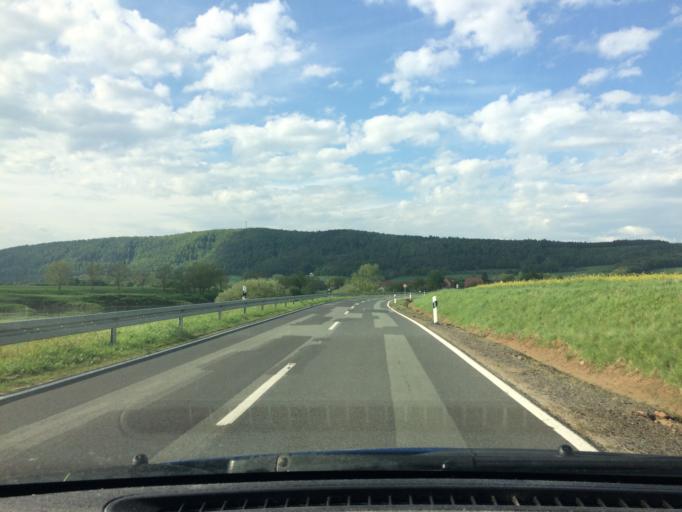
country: DE
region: Lower Saxony
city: Bodenfelde
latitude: 51.5825
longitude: 9.5945
